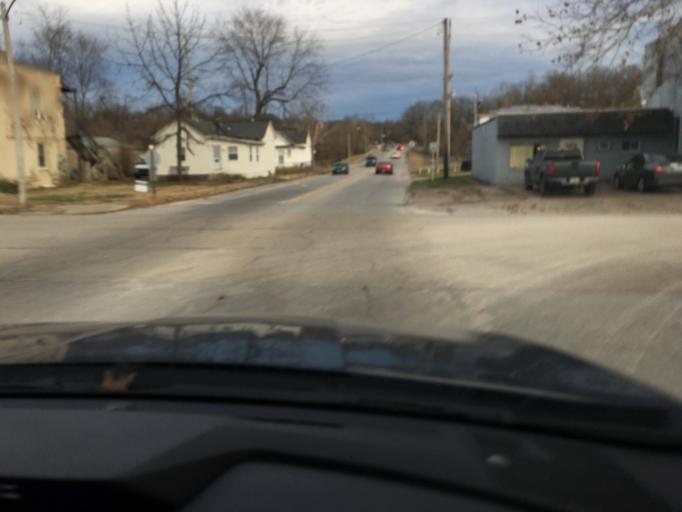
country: US
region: Missouri
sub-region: Jefferson County
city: De Soto
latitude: 38.1342
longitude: -90.5552
